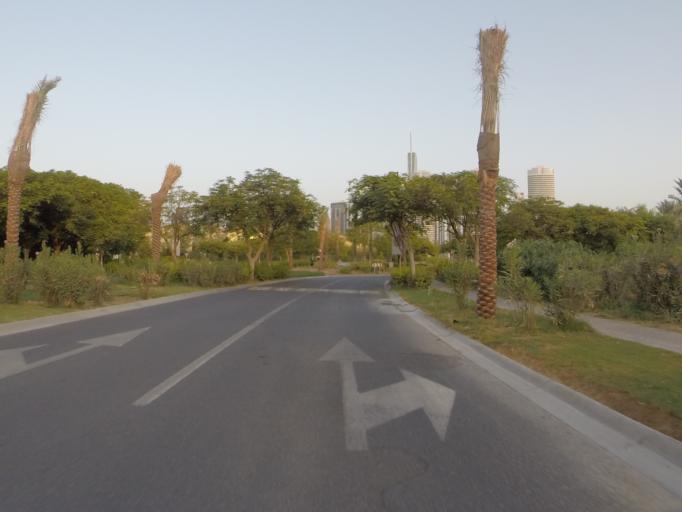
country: AE
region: Dubai
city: Dubai
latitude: 25.0636
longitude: 55.1521
